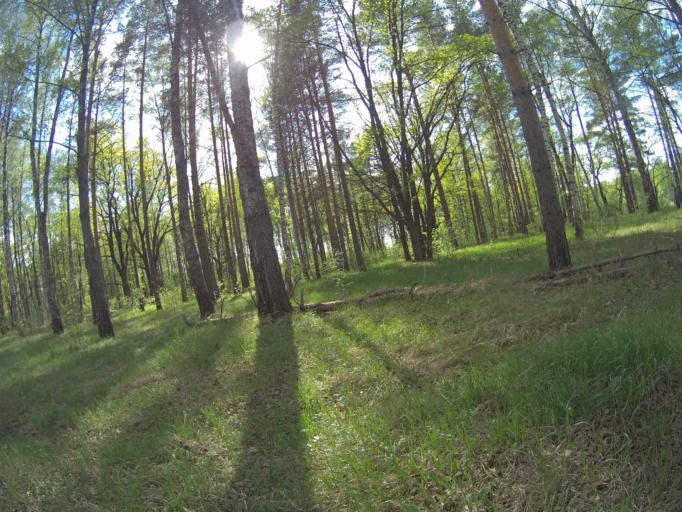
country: RU
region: Vladimir
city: Raduzhnyy
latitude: 56.0488
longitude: 40.3762
